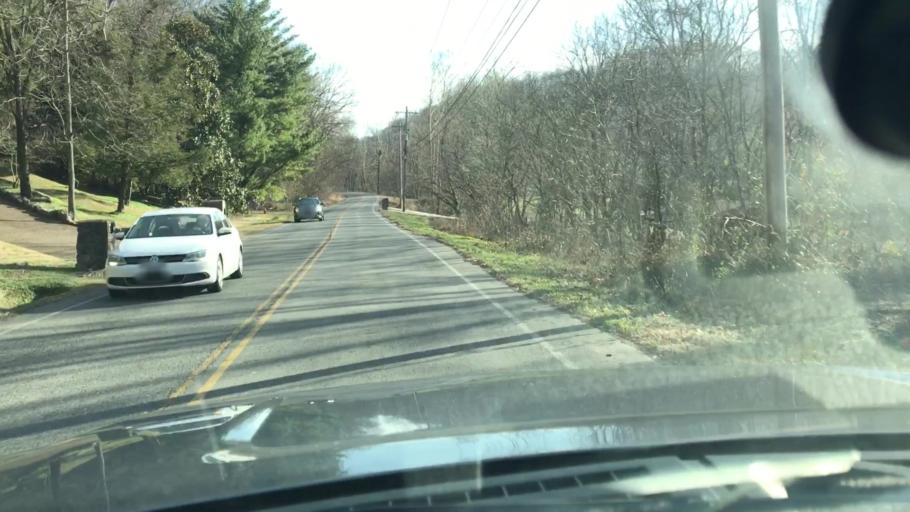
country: US
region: Tennessee
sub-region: Davidson County
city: Forest Hills
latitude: 36.0089
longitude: -86.8449
